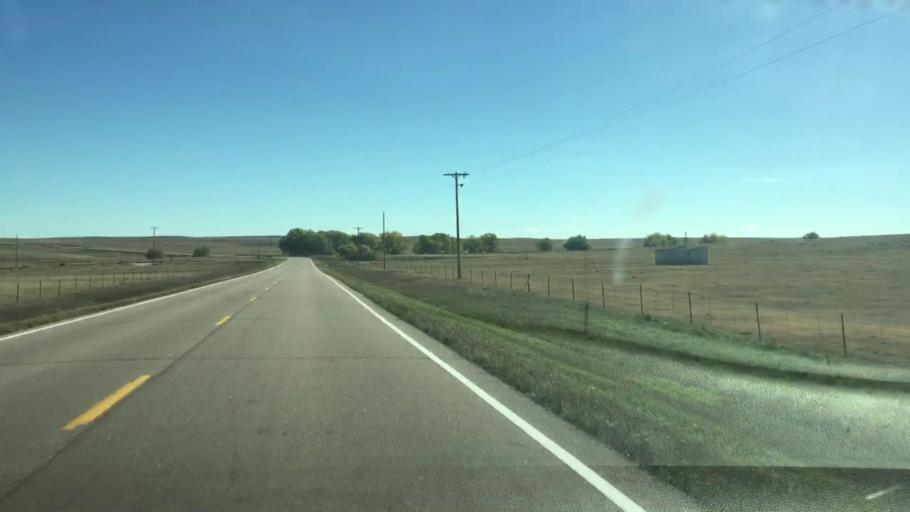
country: US
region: Colorado
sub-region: Lincoln County
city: Limon
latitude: 39.2735
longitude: -104.0152
